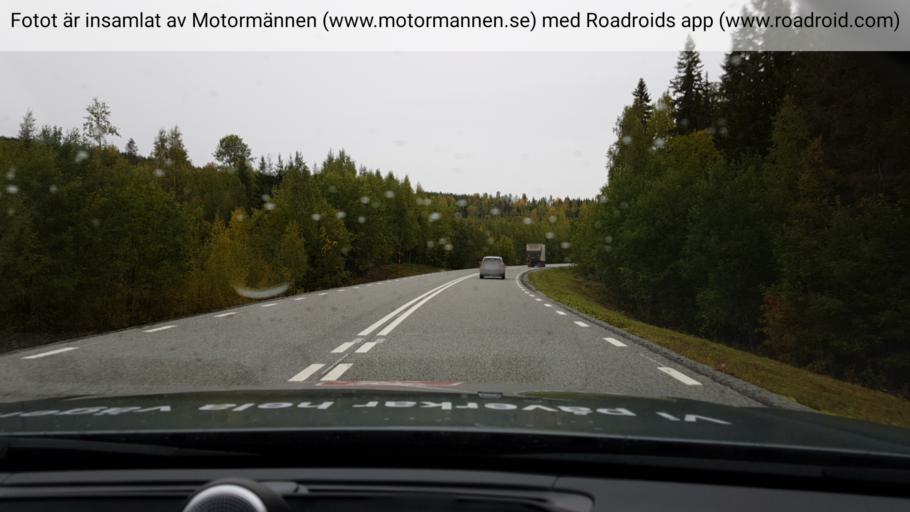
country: SE
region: Jaemtland
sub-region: Stroemsunds Kommun
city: Stroemsund
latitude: 64.0914
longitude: 15.5684
